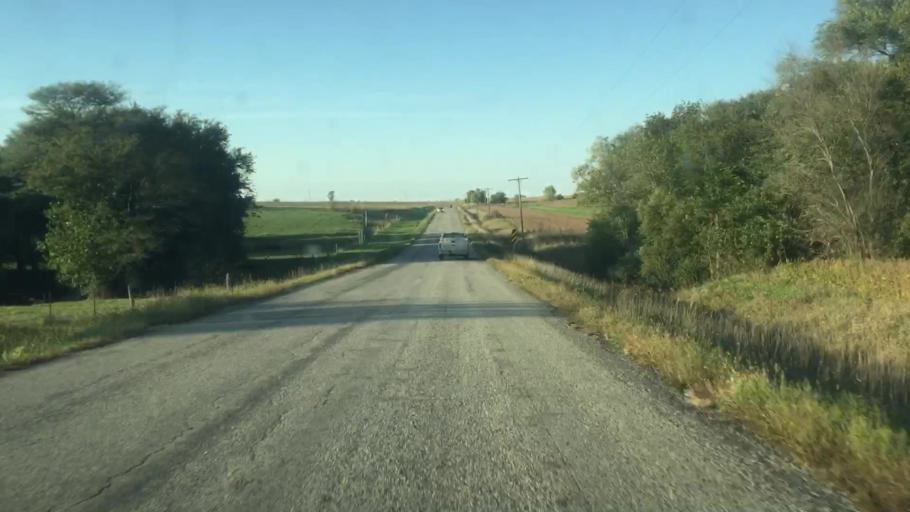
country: US
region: Kansas
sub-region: Brown County
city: Horton
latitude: 39.5591
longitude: -95.4021
